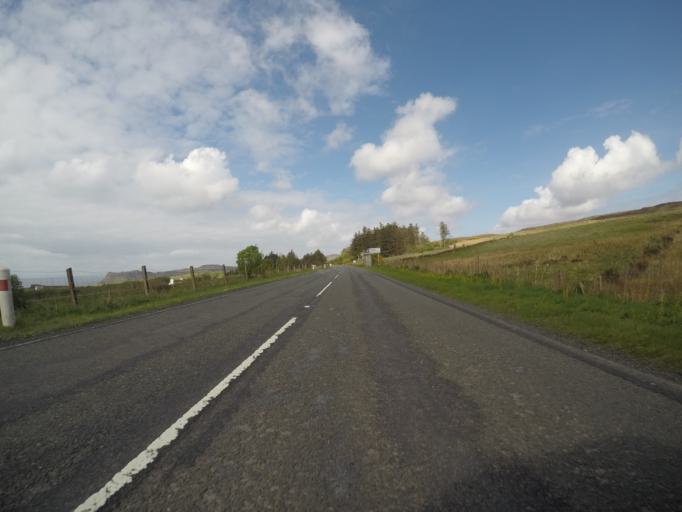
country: GB
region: Scotland
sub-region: Highland
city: Portree
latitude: 57.5669
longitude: -6.3647
